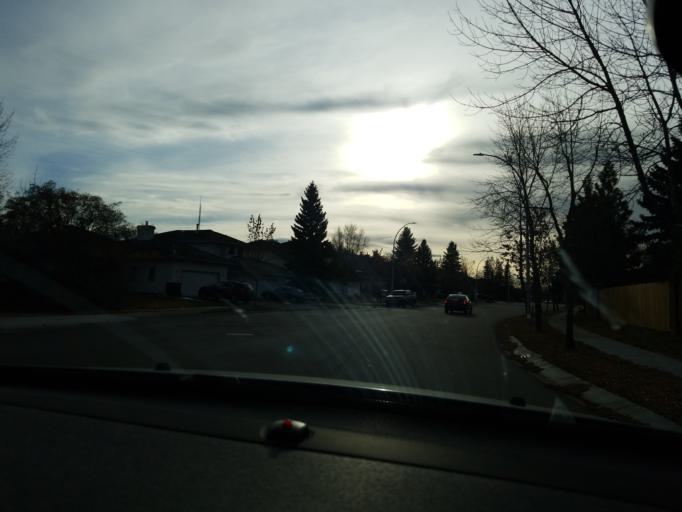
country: CA
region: Alberta
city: Sherwood Park
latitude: 53.5233
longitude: -113.2750
